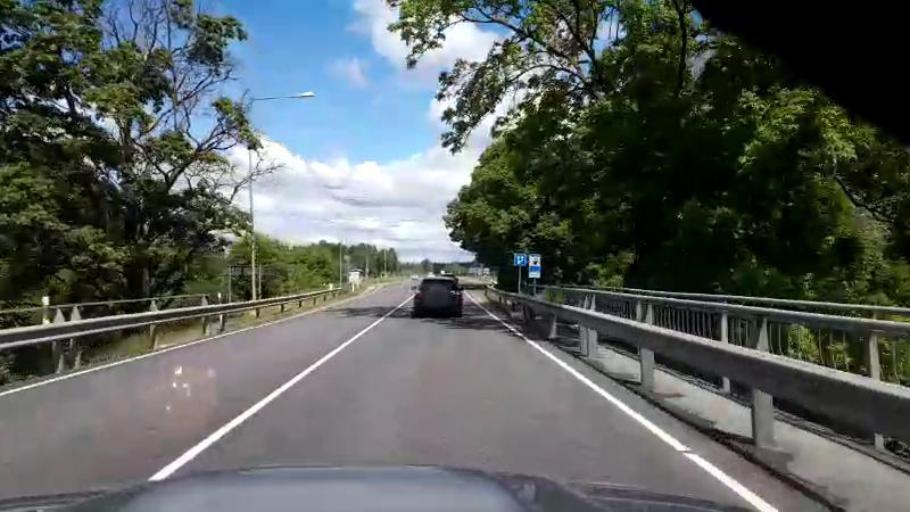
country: EE
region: Paernumaa
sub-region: Sauga vald
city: Sauga
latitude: 58.4479
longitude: 24.5005
